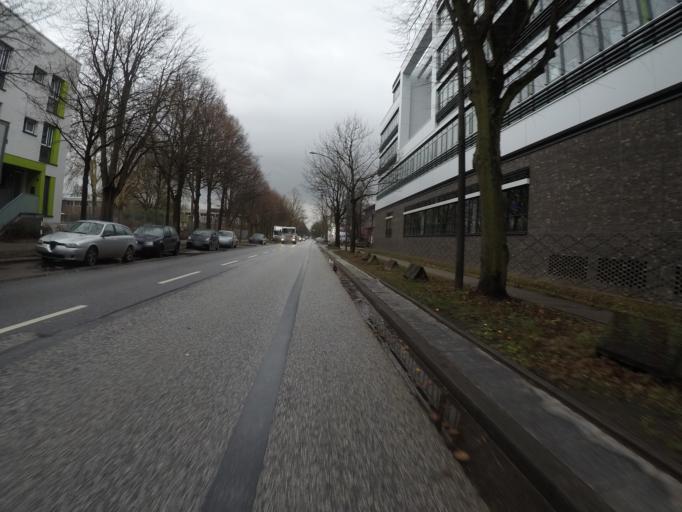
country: DE
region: Hamburg
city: Kleiner Grasbrook
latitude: 53.4960
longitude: 9.9908
